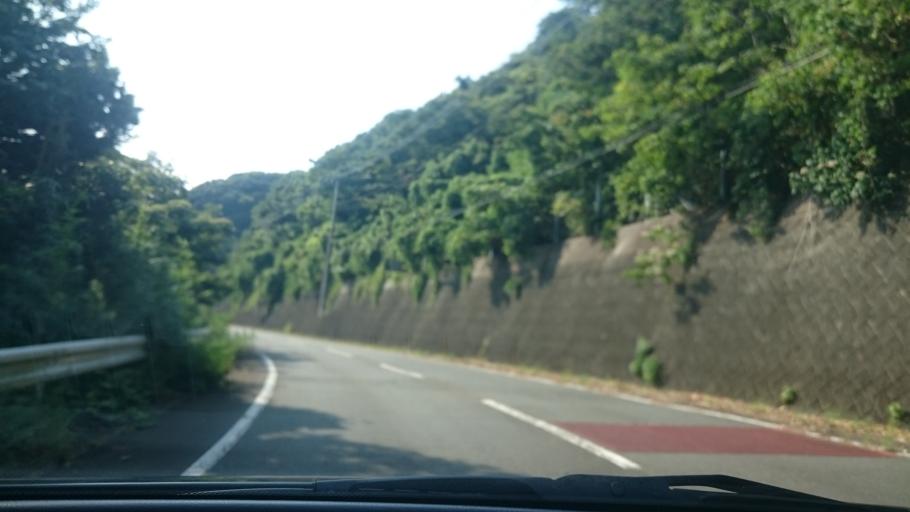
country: JP
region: Shizuoka
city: Heda
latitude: 35.0004
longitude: 138.7867
